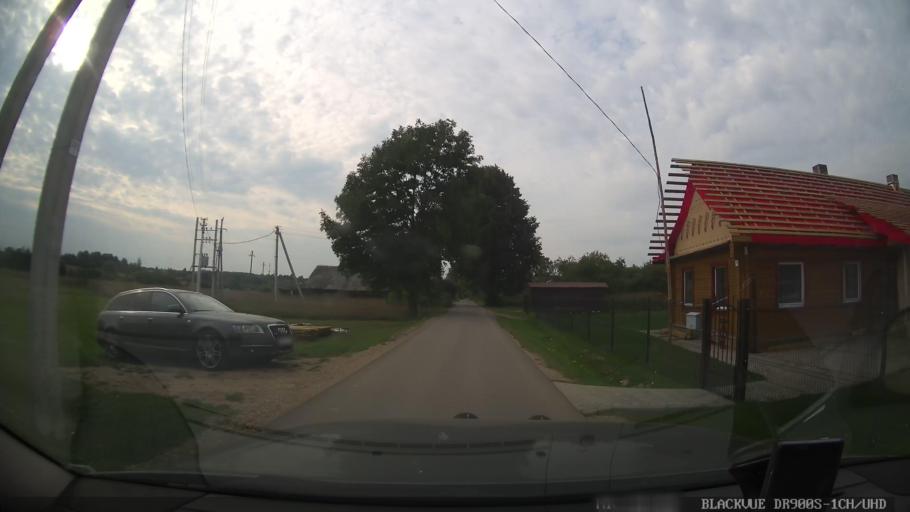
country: LT
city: Skaidiskes
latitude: 54.5335
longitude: 25.6632
